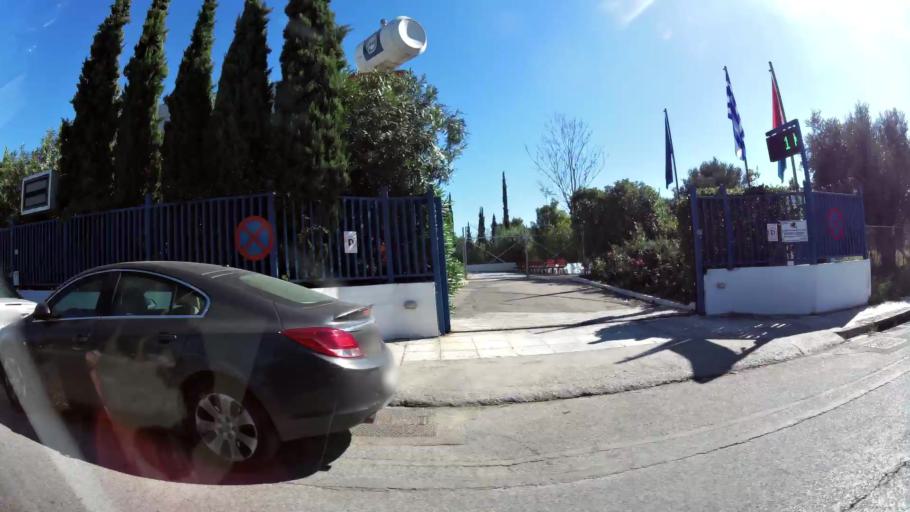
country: GR
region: Attica
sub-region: Nomarchia Athinas
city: Marousi
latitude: 38.0381
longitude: 23.8074
